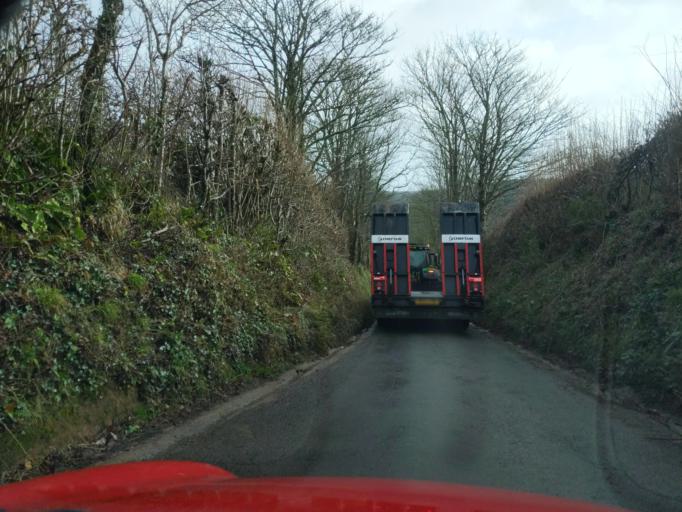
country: GB
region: England
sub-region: Devon
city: Ivybridge
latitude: 50.3543
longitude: -3.9291
